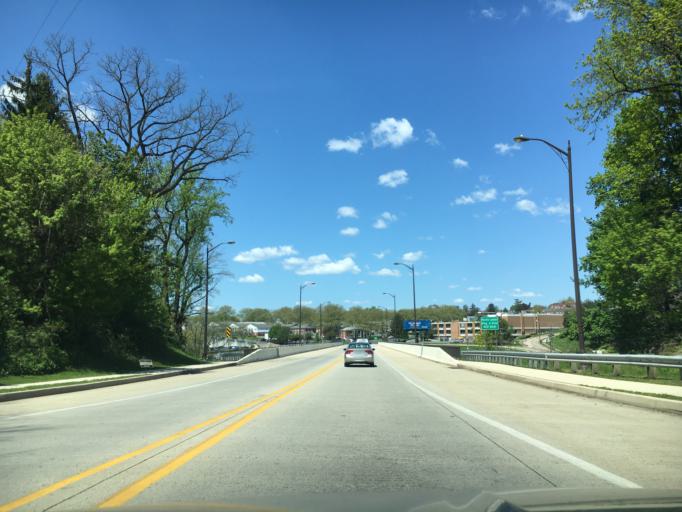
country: US
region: Pennsylvania
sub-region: Lehigh County
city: Allentown
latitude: 40.5907
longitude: -75.4812
